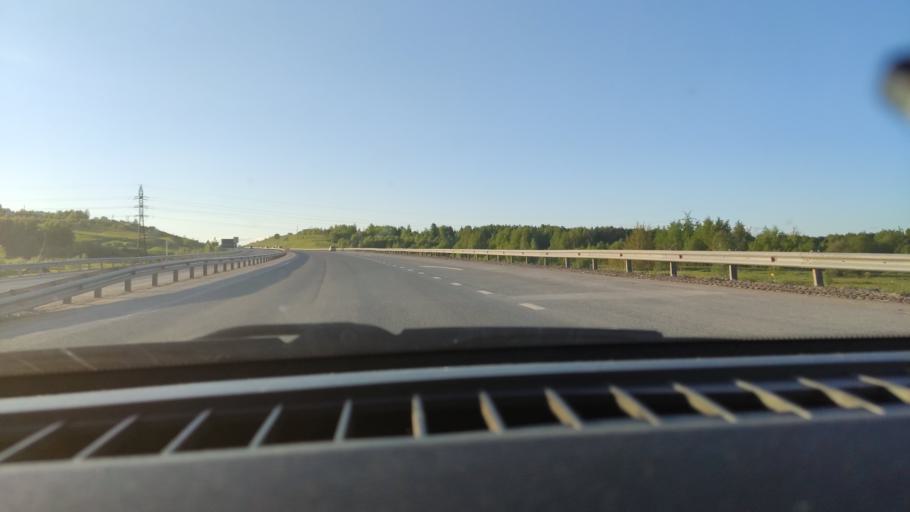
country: RU
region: Perm
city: Polazna
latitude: 58.1895
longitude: 56.4111
